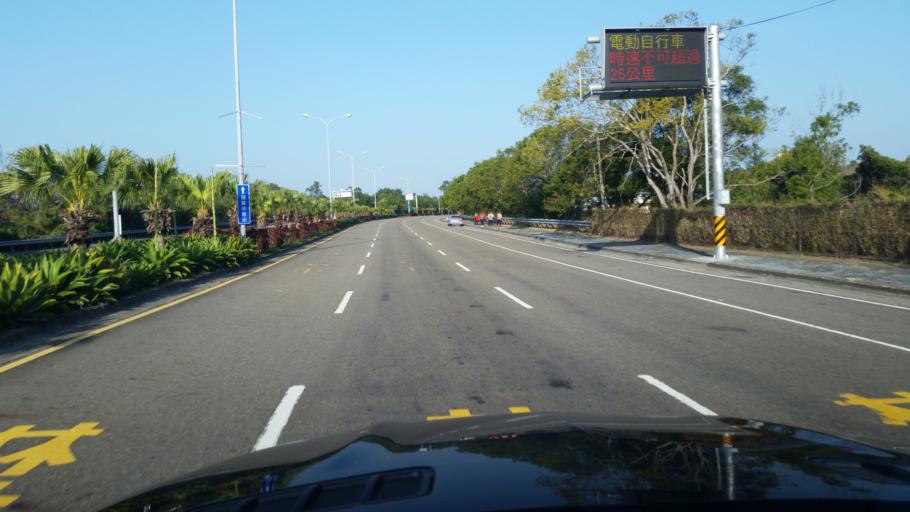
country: TW
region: Taiwan
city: Fengyuan
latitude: 24.3153
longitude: 120.6975
